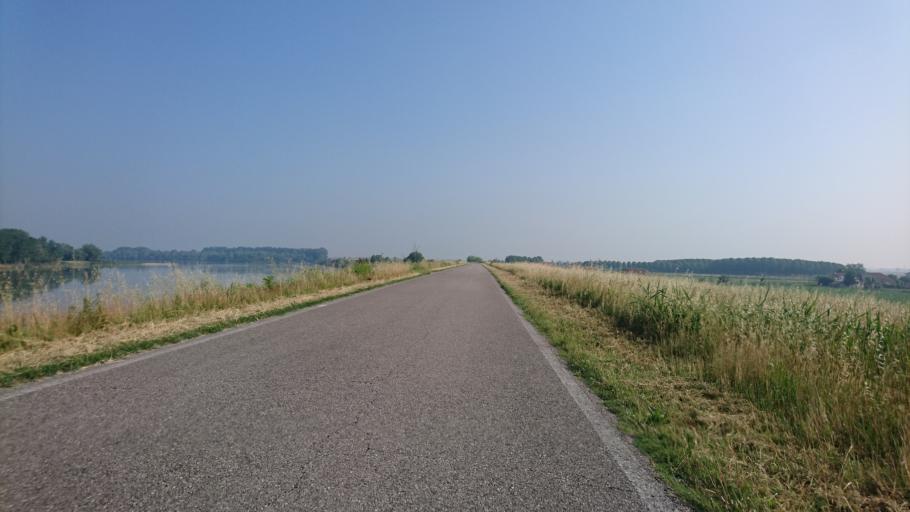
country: IT
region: Veneto
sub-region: Provincia di Rovigo
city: Castelnovo Bariano
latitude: 45.0445
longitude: 11.2727
